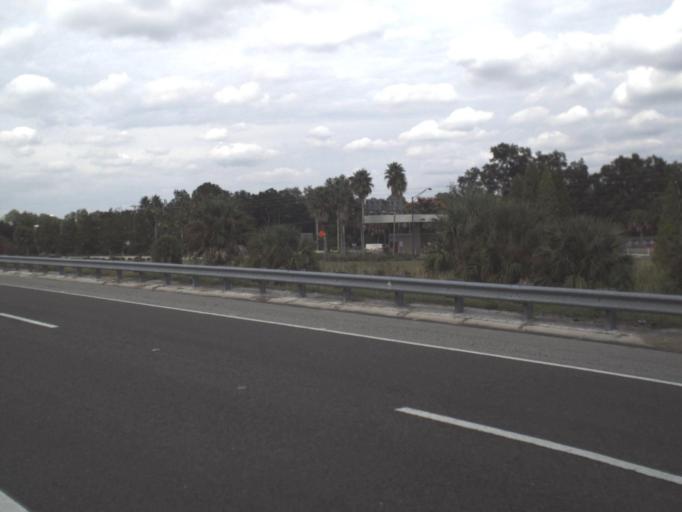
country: US
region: Florida
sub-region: Polk County
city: Medulla
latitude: 27.9953
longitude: -81.9534
